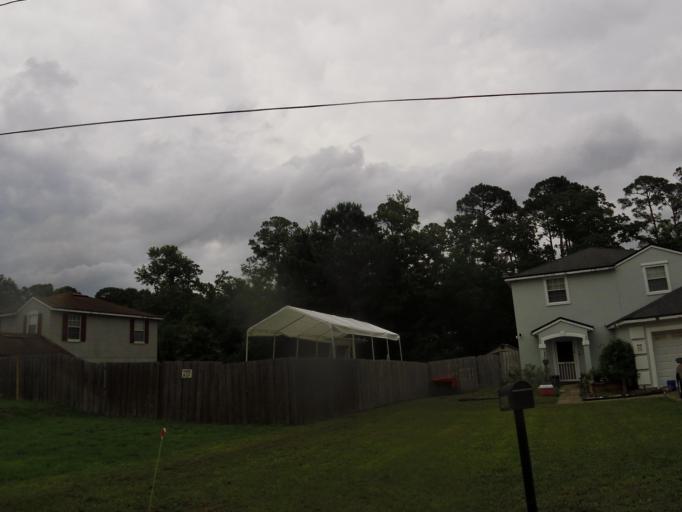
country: US
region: Florida
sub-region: Duval County
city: Jacksonville
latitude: 30.2729
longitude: -81.5396
